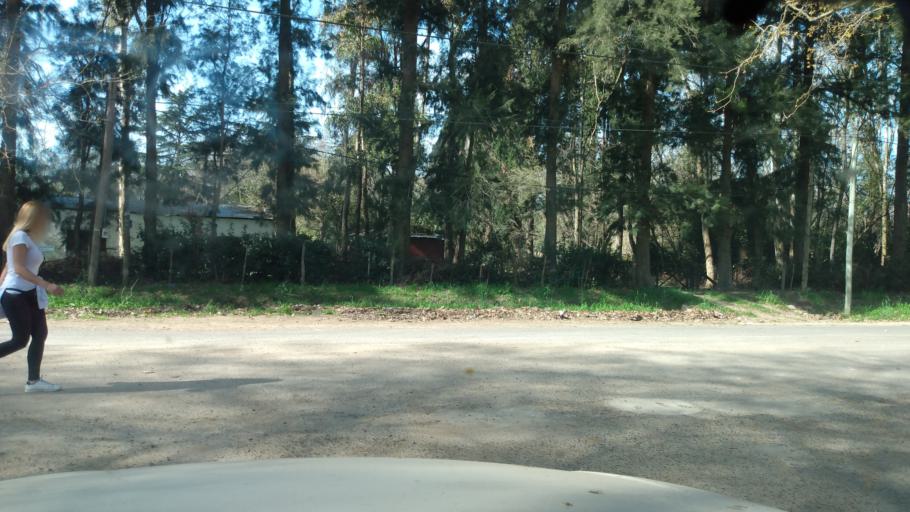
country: AR
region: Buenos Aires
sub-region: Partido de Lujan
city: Lujan
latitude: -34.5917
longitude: -59.1817
